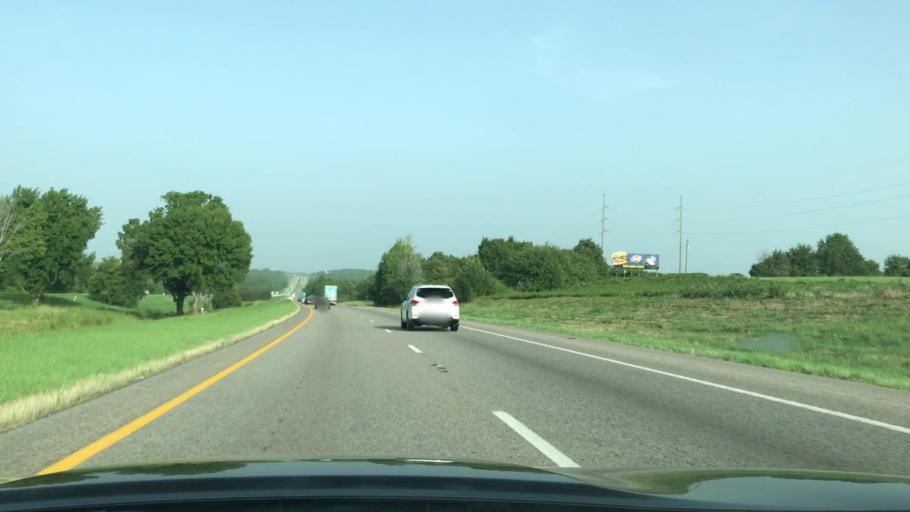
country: US
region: Texas
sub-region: Smith County
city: Hideaway
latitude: 32.4803
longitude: -95.4920
